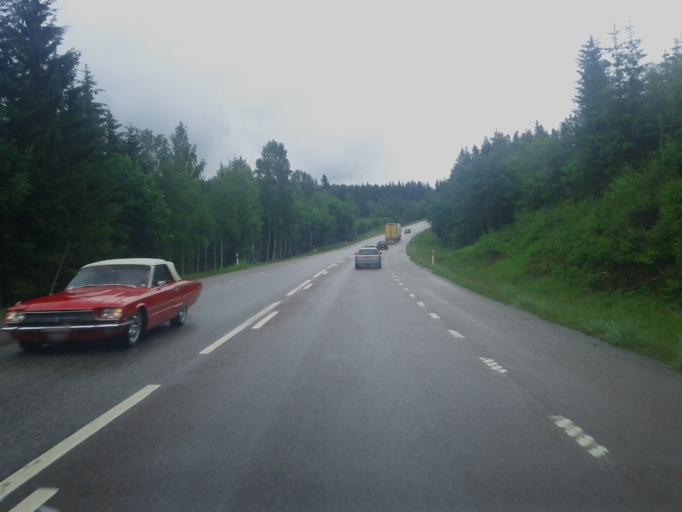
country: SE
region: Vaesternorrland
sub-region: Haernoesands Kommun
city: Haernoesand
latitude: 62.7029
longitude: 17.8592
